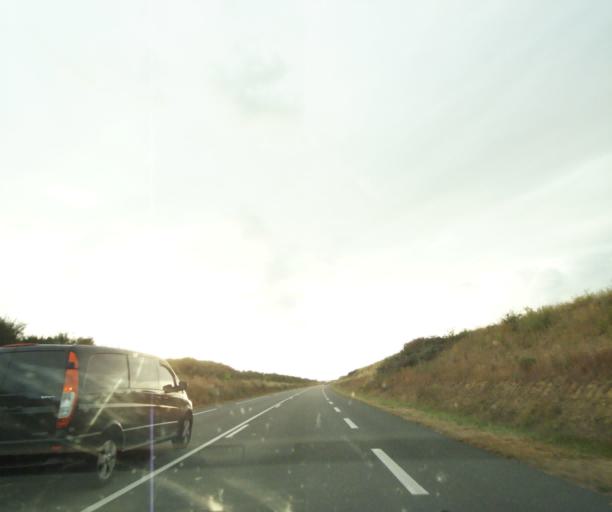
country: FR
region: Pays de la Loire
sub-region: Departement de la Vendee
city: Saint-Hilaire-de-Talmont
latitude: 46.4659
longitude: -1.6430
